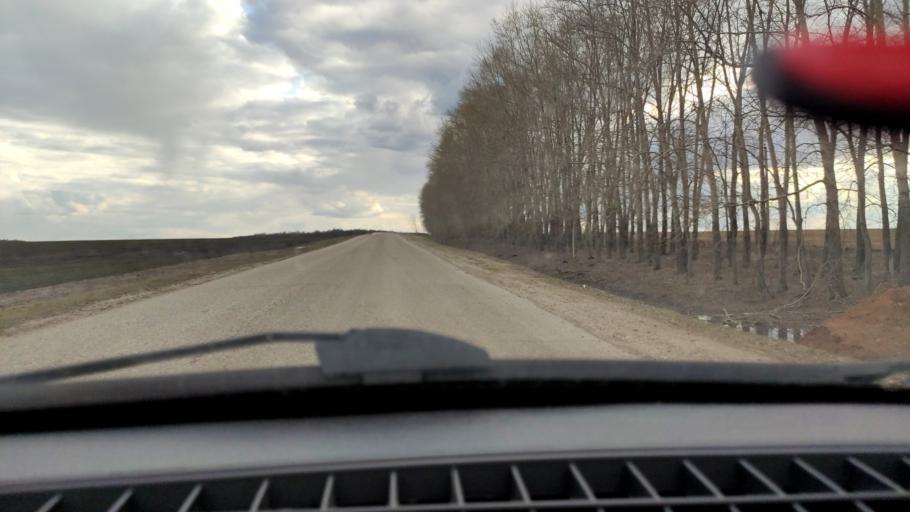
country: RU
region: Bashkortostan
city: Karmaskaly
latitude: 54.3085
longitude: 55.9407
